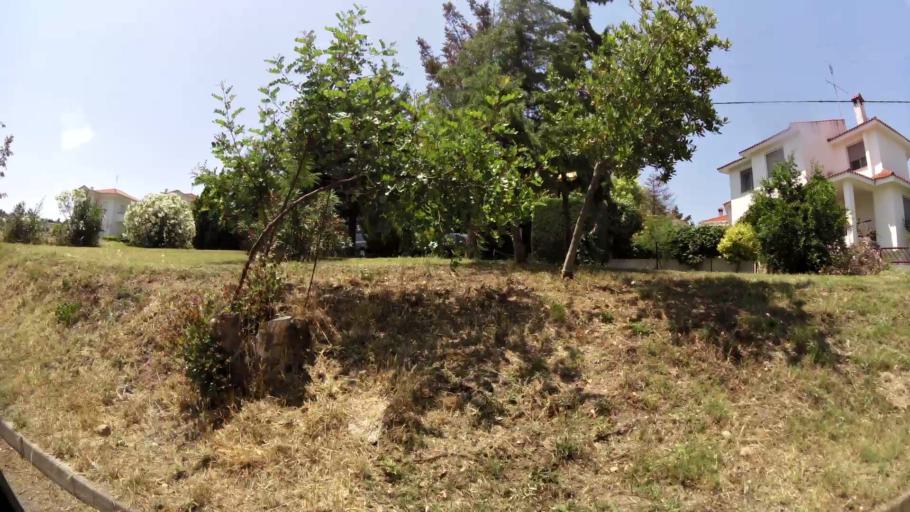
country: GR
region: Central Macedonia
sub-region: Nomos Thessalonikis
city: Plagiari
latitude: 40.4709
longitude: 22.9613
